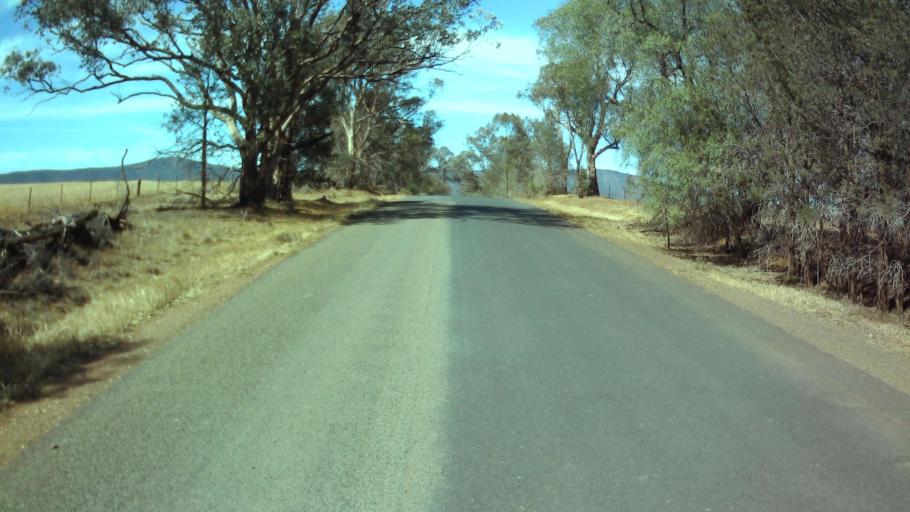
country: AU
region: New South Wales
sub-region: Weddin
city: Grenfell
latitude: -33.9341
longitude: 148.0834
